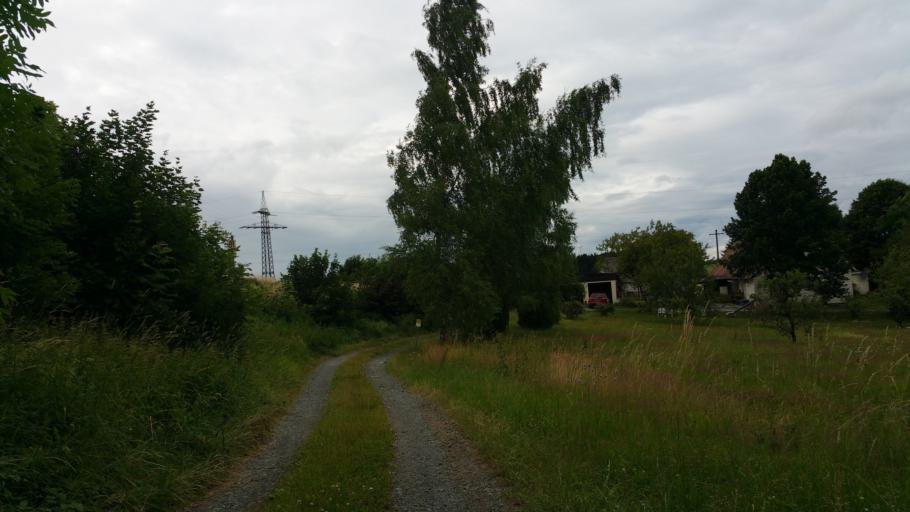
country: DE
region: Bavaria
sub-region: Upper Franconia
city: Schwarzenbach an der Saale
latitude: 50.2246
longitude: 11.9538
